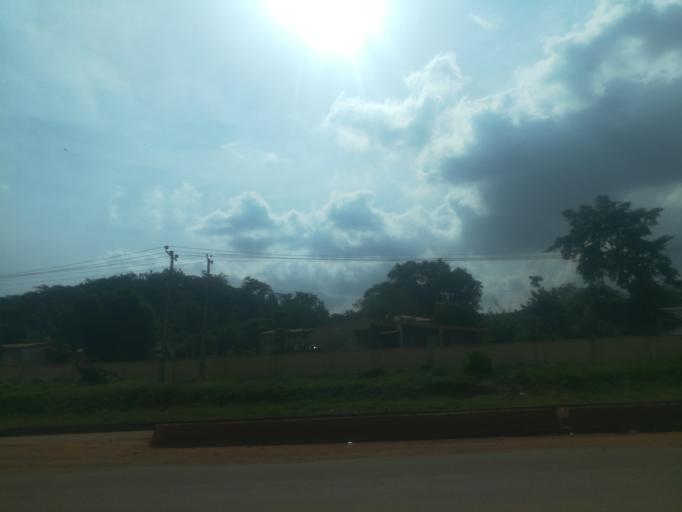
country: NG
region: Ogun
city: Abeokuta
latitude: 7.1299
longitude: 3.3549
